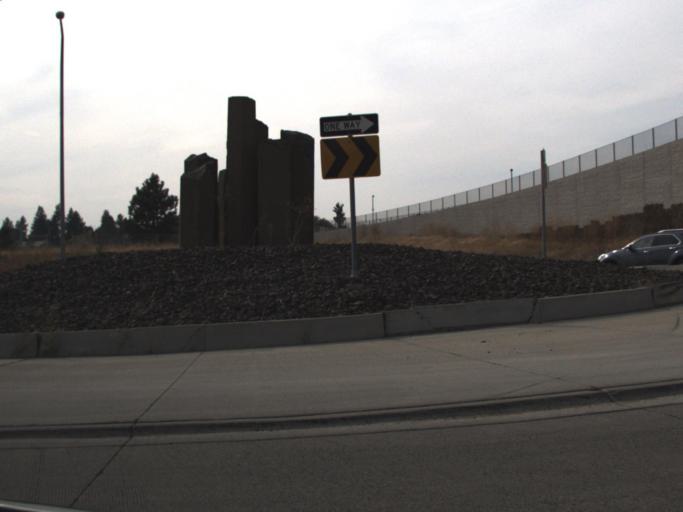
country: US
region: Washington
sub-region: Spokane County
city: Mead
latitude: 47.7731
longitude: -117.3725
